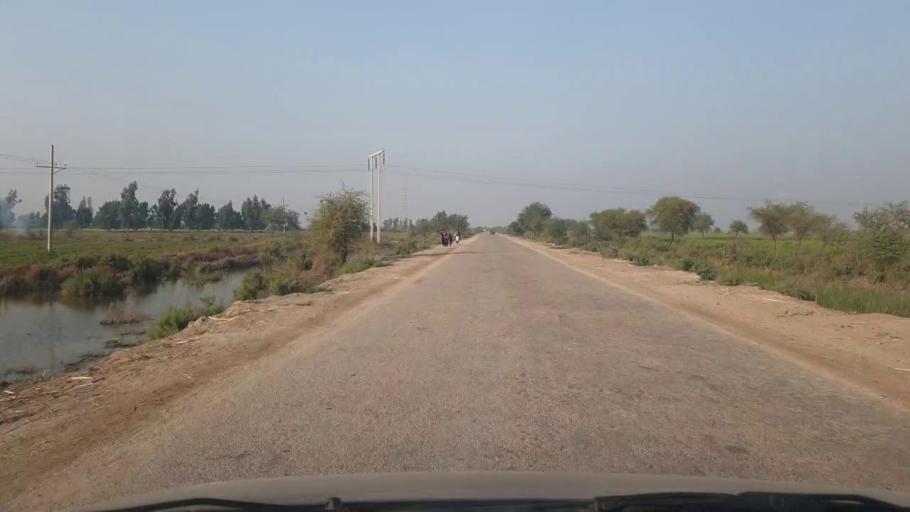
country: PK
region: Sindh
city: Mirwah Gorchani
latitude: 25.3152
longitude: 69.1643
